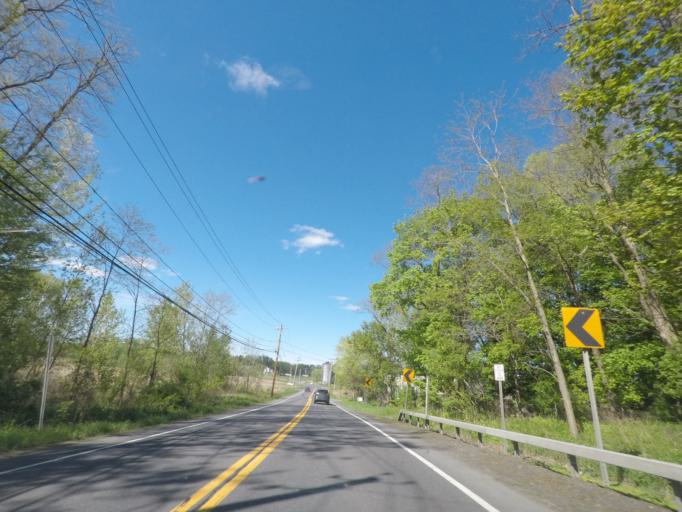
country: US
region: New York
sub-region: Albany County
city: Delmar
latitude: 42.5796
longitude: -73.7982
